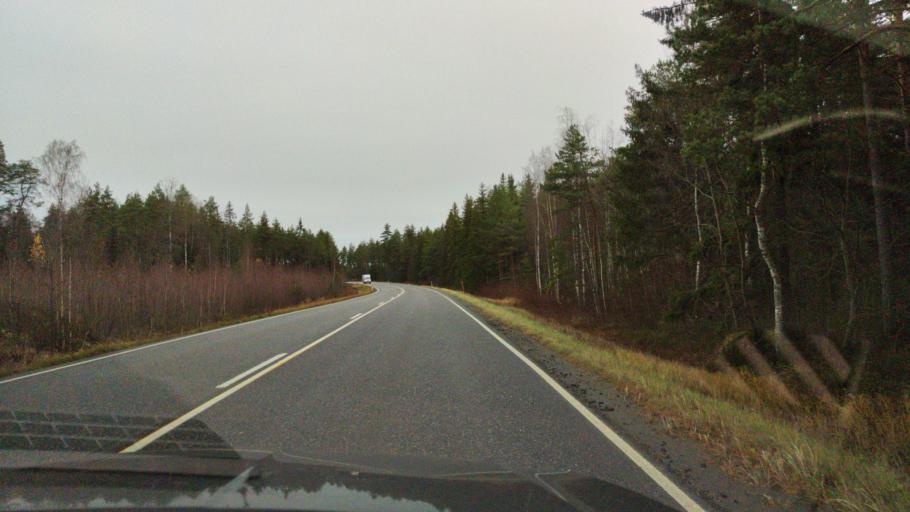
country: FI
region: Varsinais-Suomi
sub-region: Turku
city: Lieto
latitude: 60.5820
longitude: 22.4303
